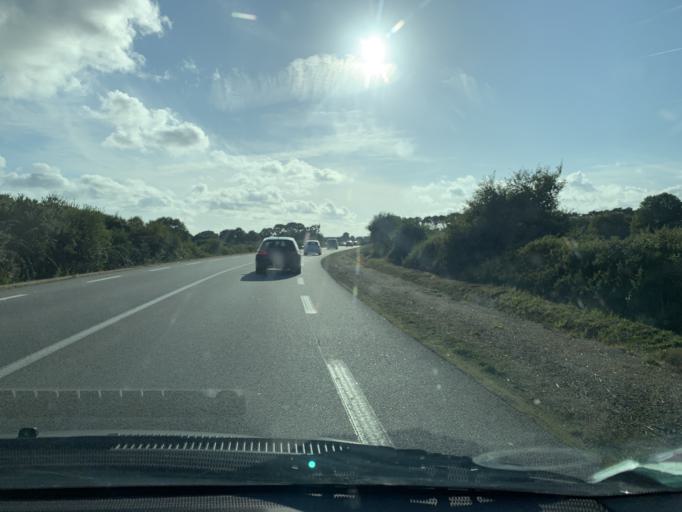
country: FR
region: Brittany
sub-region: Departement du Morbihan
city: Sarzeau
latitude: 47.5518
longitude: -2.7110
